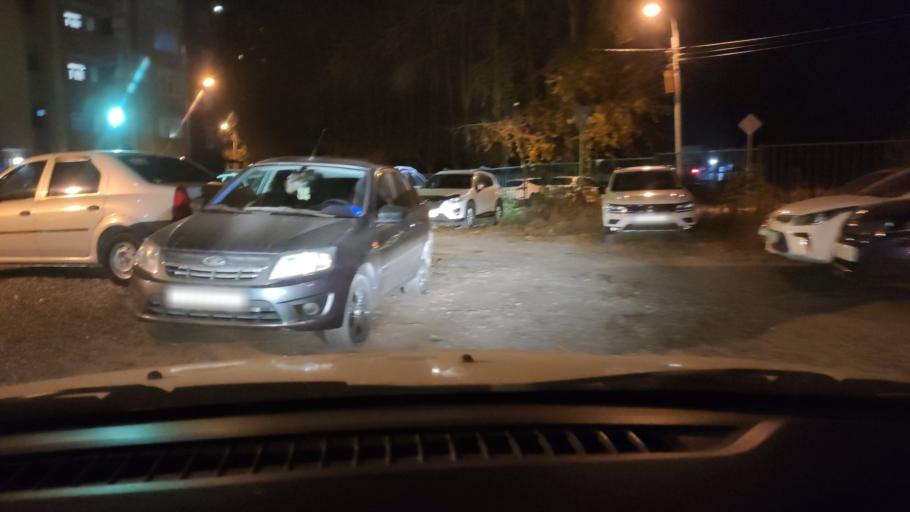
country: RU
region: Perm
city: Kondratovo
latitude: 57.9998
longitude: 56.1653
